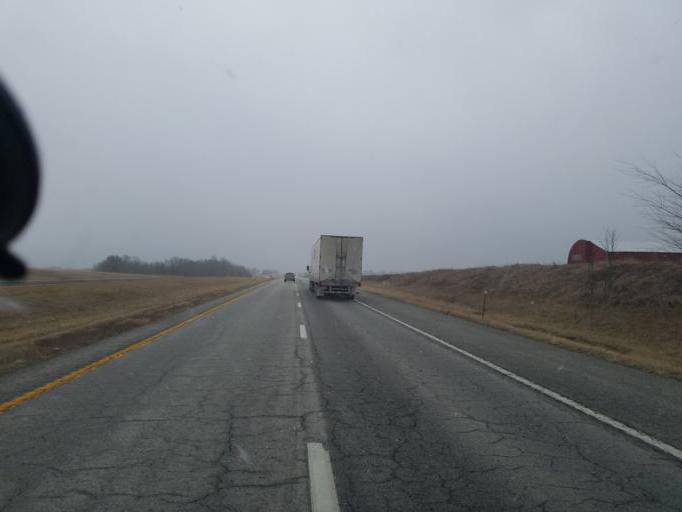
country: US
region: Missouri
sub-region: Macon County
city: La Plata
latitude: 39.9151
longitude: -92.4742
